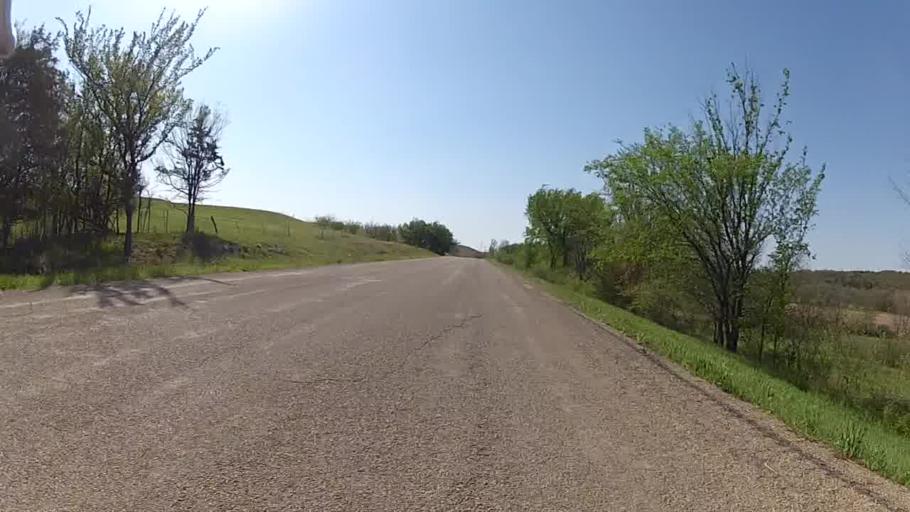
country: US
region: Kansas
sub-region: Riley County
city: Ogden
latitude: 39.0052
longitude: -96.6742
